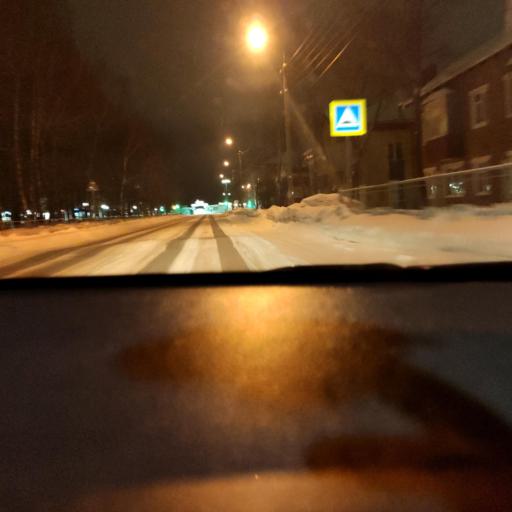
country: RU
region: Tatarstan
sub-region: Chistopol'skiy Rayon
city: Chistopol'
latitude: 55.3647
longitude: 50.6087
